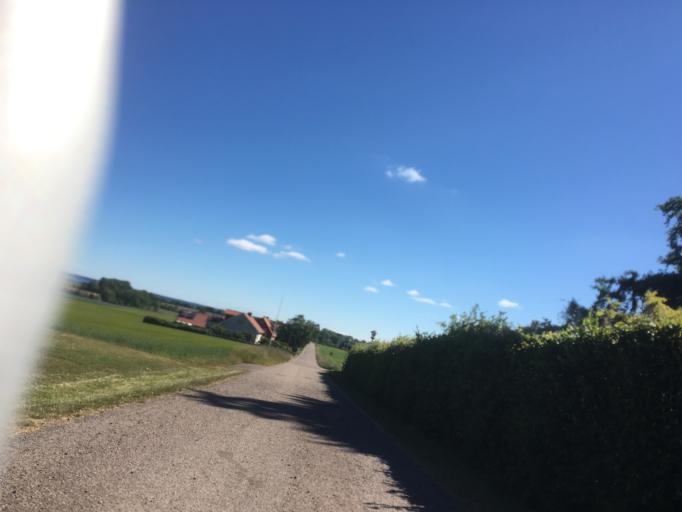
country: SE
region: Skane
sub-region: Helsingborg
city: Rydeback
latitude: 55.9107
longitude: 12.6779
